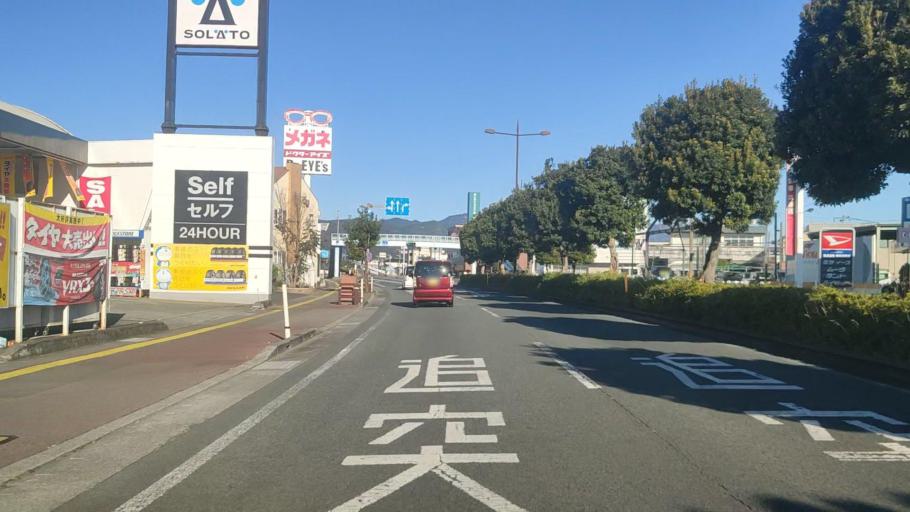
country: JP
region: Miyazaki
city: Nobeoka
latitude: 32.5782
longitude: 131.6832
